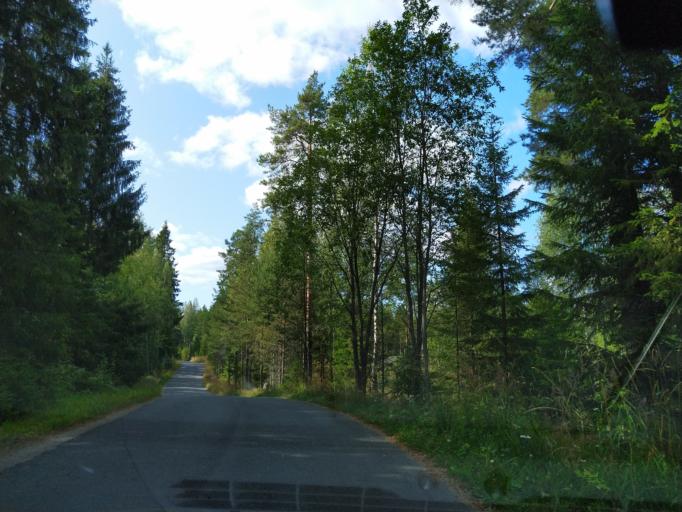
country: FI
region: Uusimaa
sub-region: Helsinki
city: Karkkila
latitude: 60.7197
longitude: 24.1808
